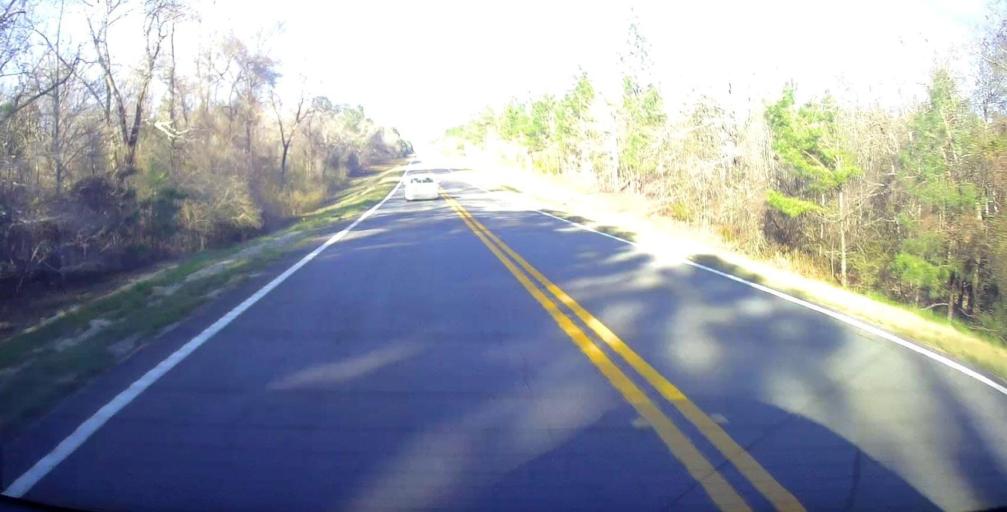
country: US
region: Georgia
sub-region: Taylor County
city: Butler
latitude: 32.5329
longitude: -84.2988
